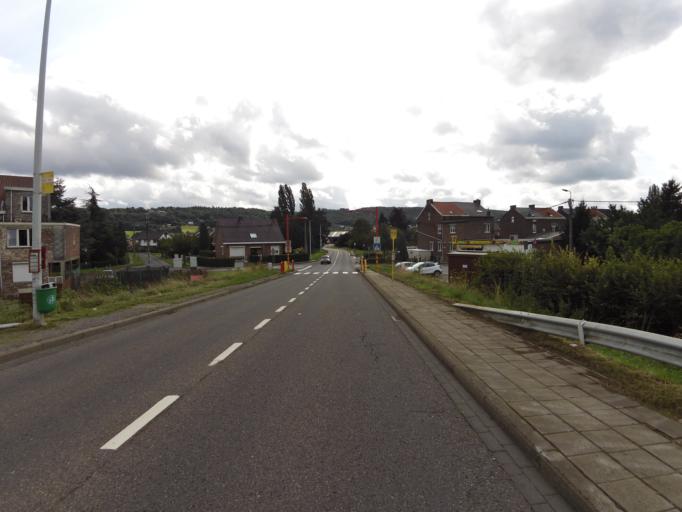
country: BE
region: Wallonia
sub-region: Province de Liege
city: Amay
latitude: 50.5474
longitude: 5.3251
